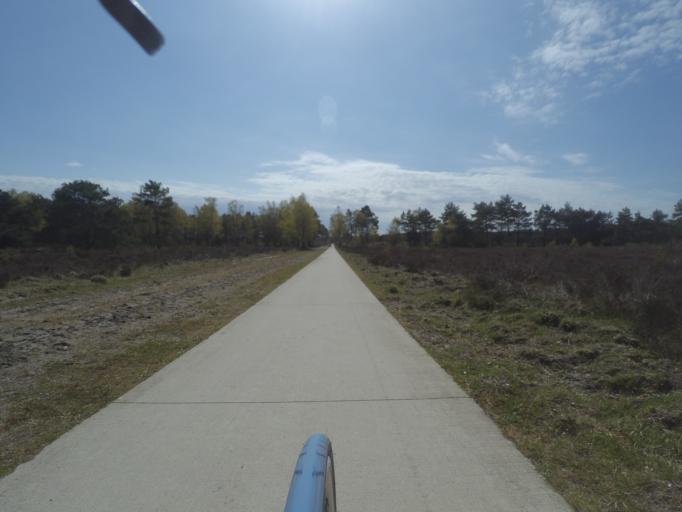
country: NL
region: Gelderland
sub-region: Gemeente Epe
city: Emst
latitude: 52.3255
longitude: 5.8862
